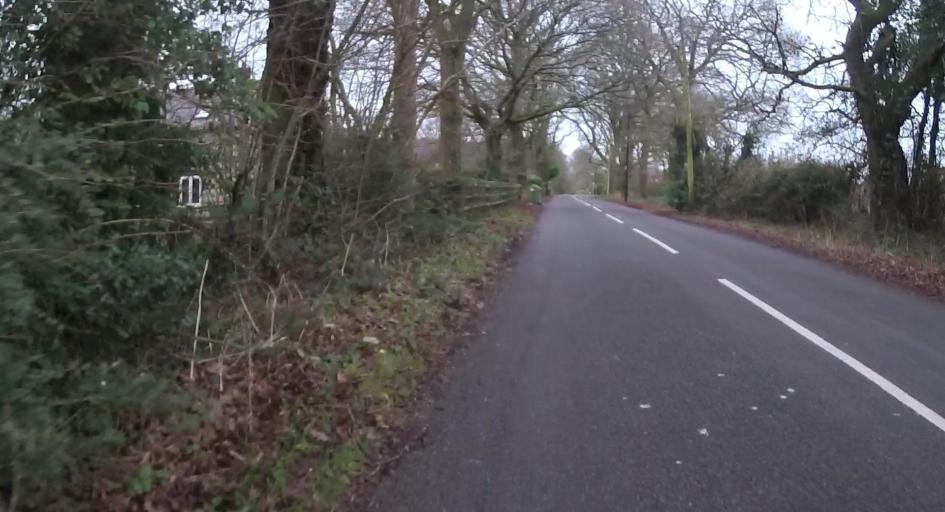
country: GB
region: England
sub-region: Hampshire
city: Four Marks
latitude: 51.1085
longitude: -1.0324
